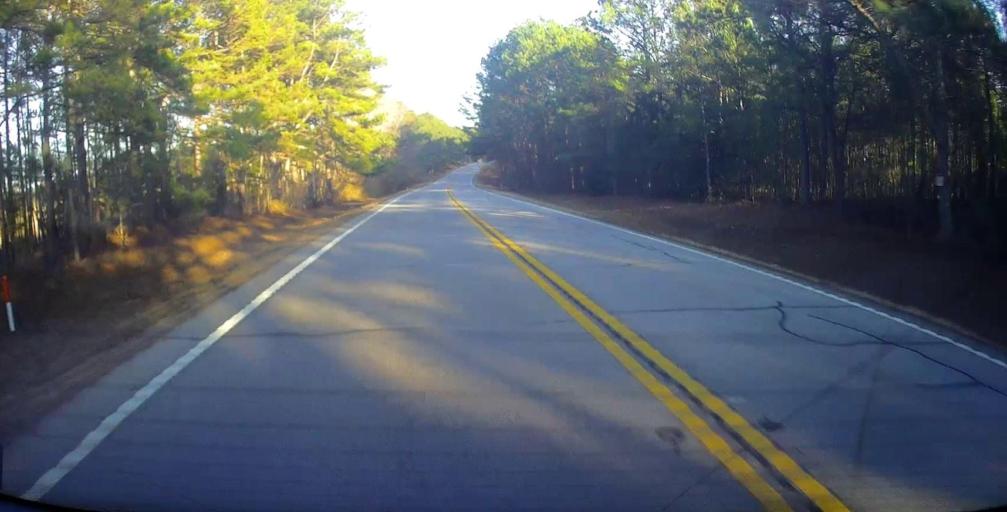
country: US
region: Georgia
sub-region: Harris County
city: Pine Mountain
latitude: 32.8555
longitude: -84.9468
